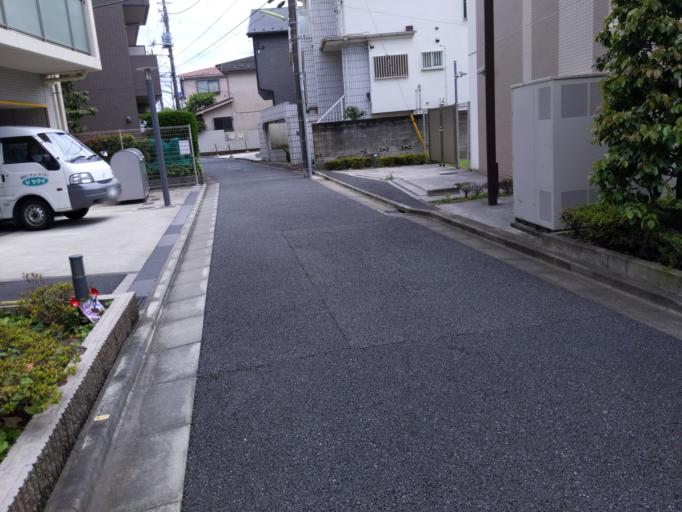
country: JP
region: Tokyo
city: Tokyo
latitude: 35.6523
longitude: 139.6424
